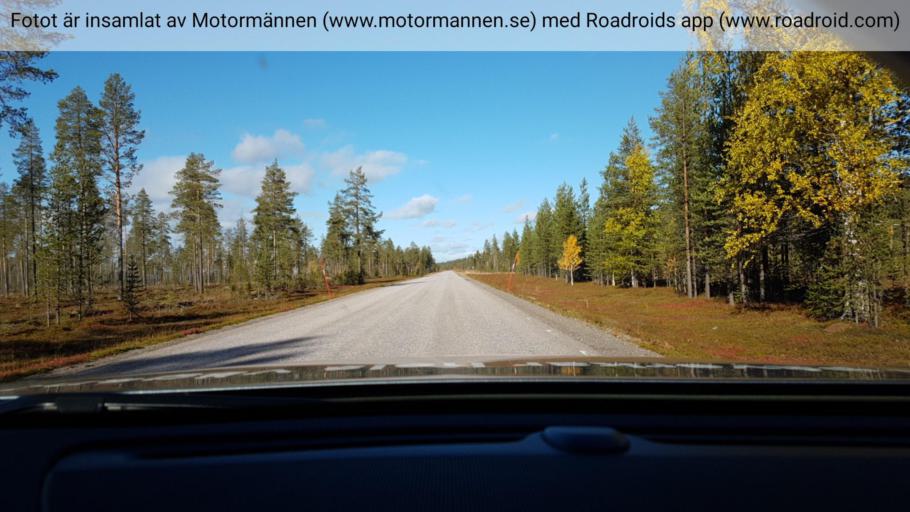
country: SE
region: Norrbotten
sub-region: Arvidsjaurs Kommun
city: Arvidsjaur
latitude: 65.6885
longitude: 18.7874
